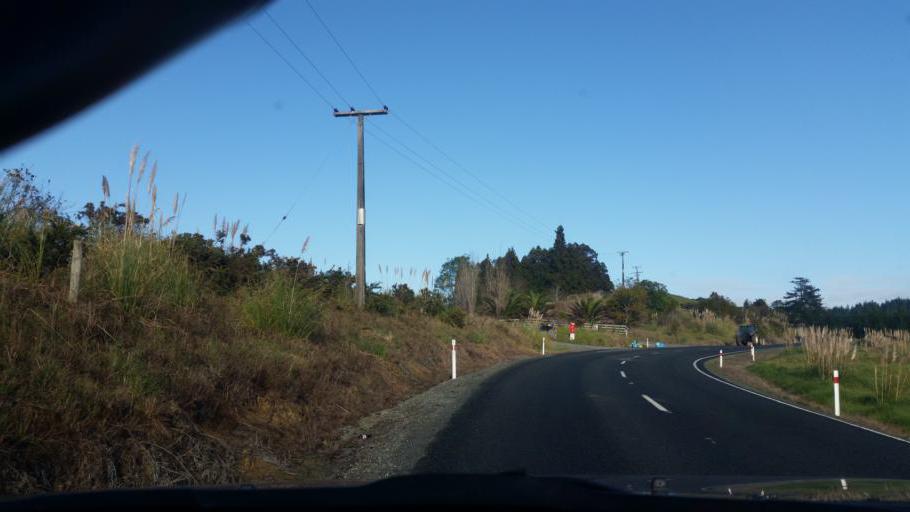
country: NZ
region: Auckland
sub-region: Auckland
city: Wellsford
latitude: -36.2209
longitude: 174.4615
